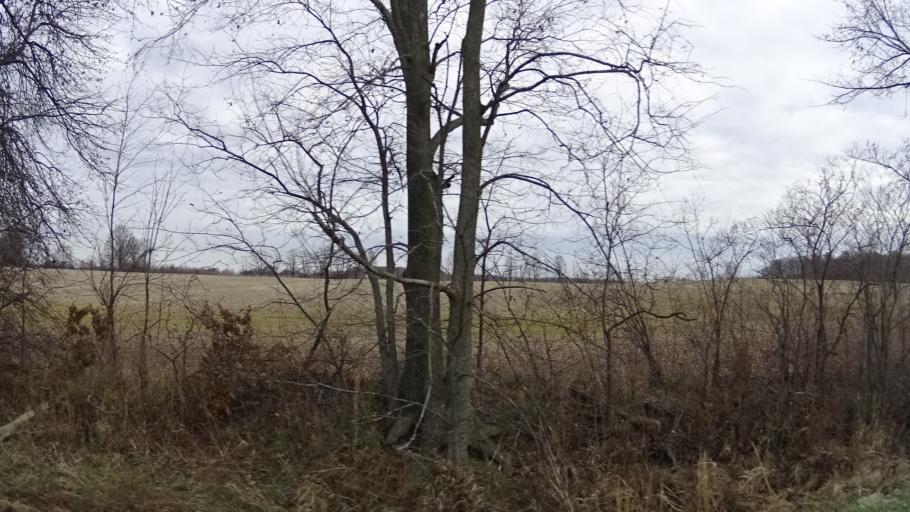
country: US
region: Ohio
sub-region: Lorain County
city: Camden
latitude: 41.2706
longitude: -82.3420
